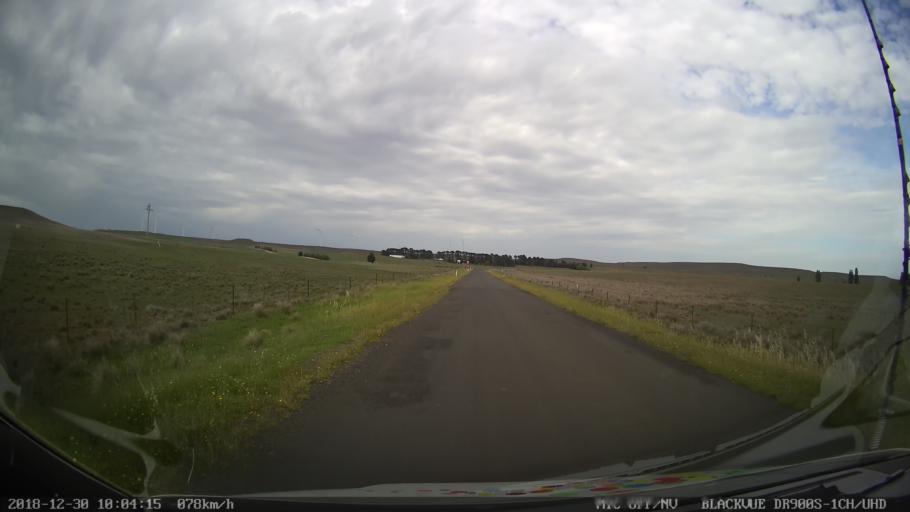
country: AU
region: New South Wales
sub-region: Cooma-Monaro
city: Cooma
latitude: -36.5203
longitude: 149.1481
